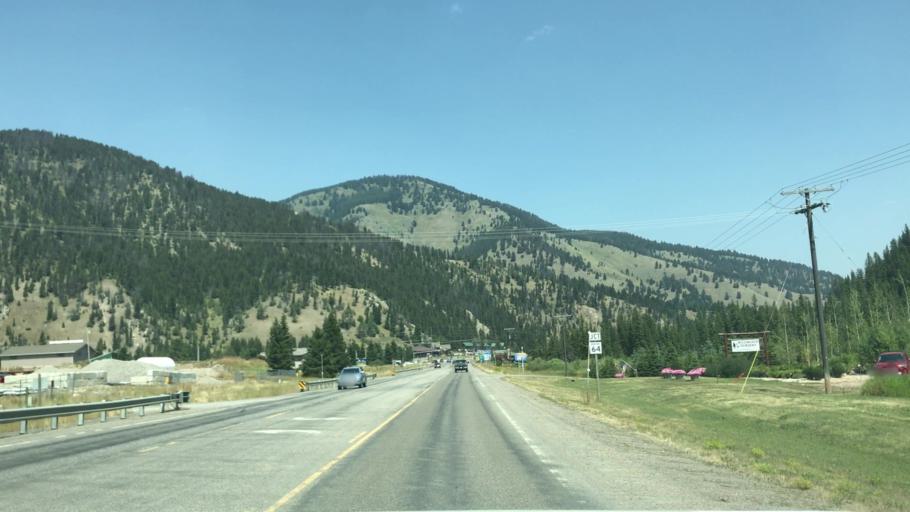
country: US
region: Montana
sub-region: Gallatin County
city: Big Sky
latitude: 45.2605
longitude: -111.2543
